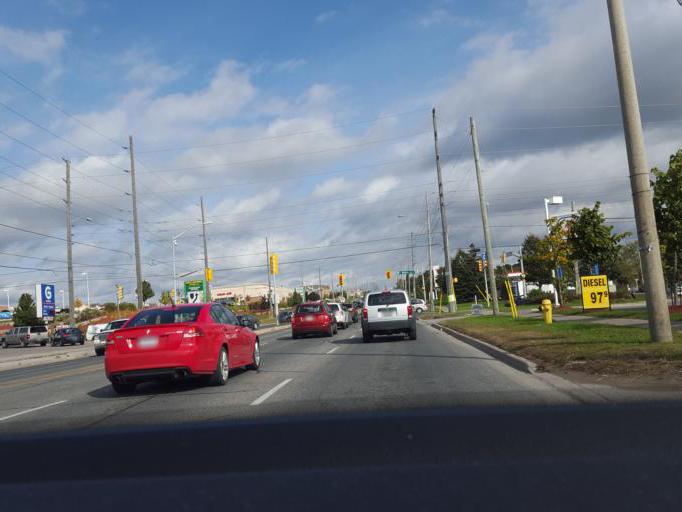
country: CA
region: Ontario
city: Oshawa
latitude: 43.9371
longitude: -78.8601
